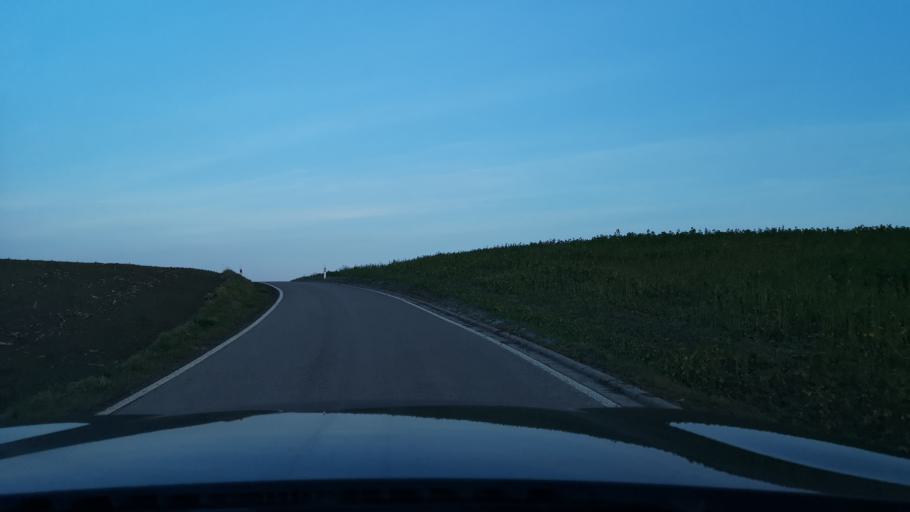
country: DE
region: Baden-Wuerttemberg
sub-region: Regierungsbezirk Stuttgart
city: Kaisersbach
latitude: 48.9411
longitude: 9.6846
